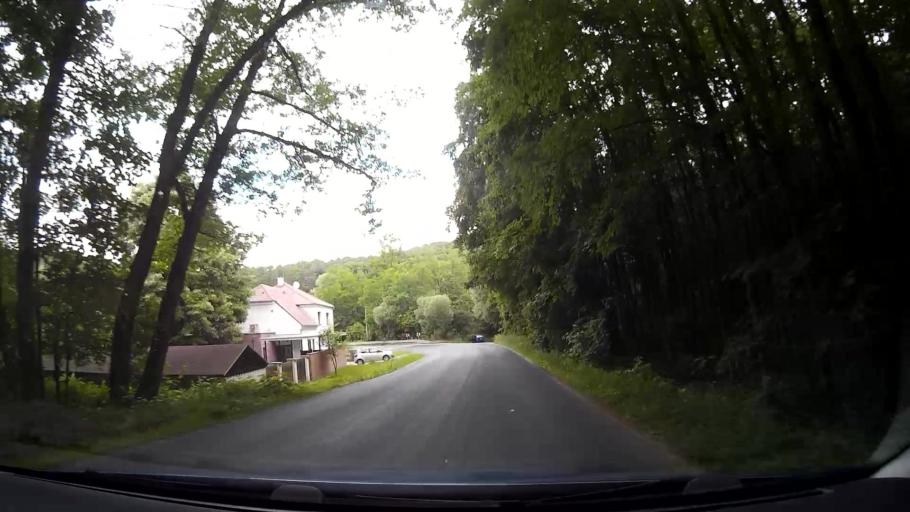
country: CZ
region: South Moravian
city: Orechov
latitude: 49.1332
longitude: 16.5294
